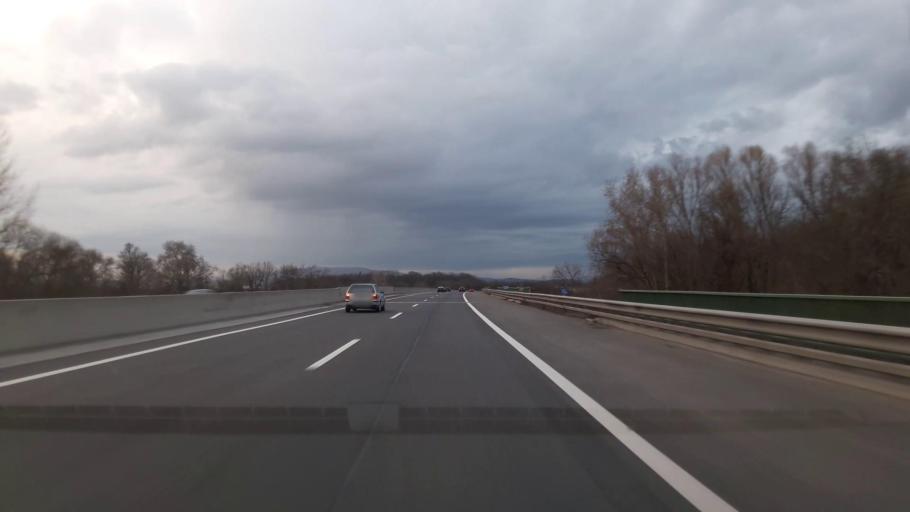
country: AT
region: Lower Austria
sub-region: Politischer Bezirk Baden
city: Ebreichsdorf
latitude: 47.9430
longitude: 16.3733
